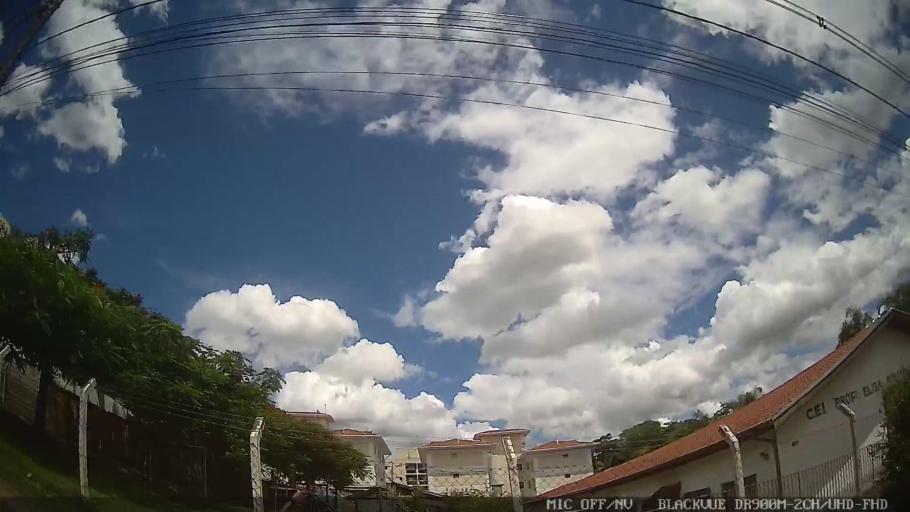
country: BR
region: Sao Paulo
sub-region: Jaguariuna
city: Jaguariuna
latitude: -22.6912
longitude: -46.9893
